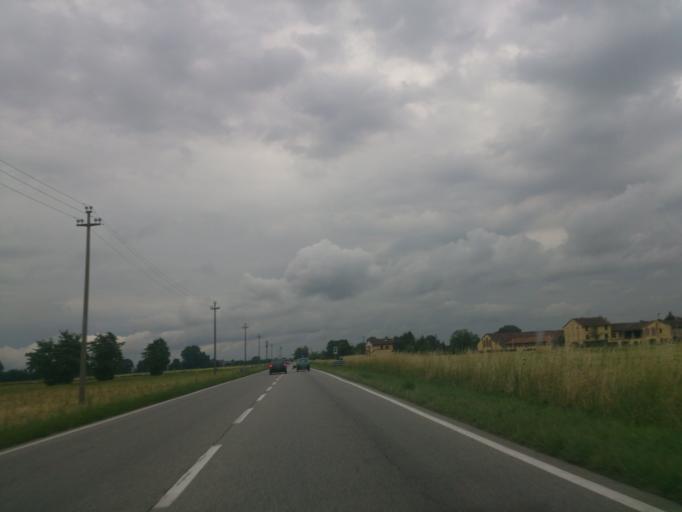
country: IT
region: Lombardy
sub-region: Citta metropolitana di Milano
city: Bettola-Zeloforomagno
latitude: 45.4183
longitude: 9.3135
